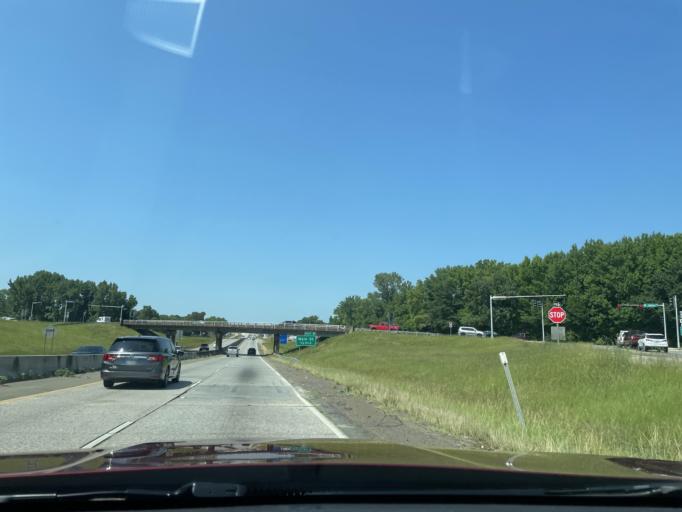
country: US
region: Arkansas
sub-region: Pulaski County
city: Jacksonville
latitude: 34.8762
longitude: -92.1174
